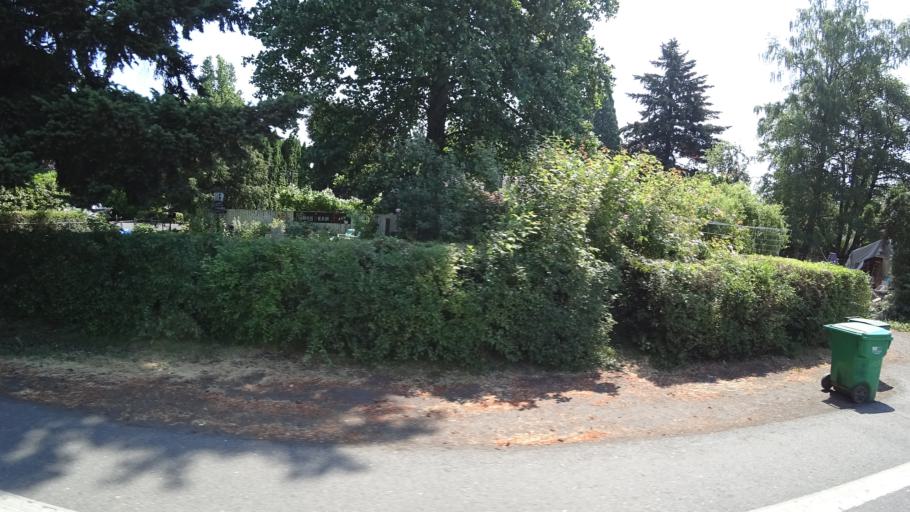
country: US
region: Oregon
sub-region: Clackamas County
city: Oatfield
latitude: 45.4454
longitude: -122.5990
